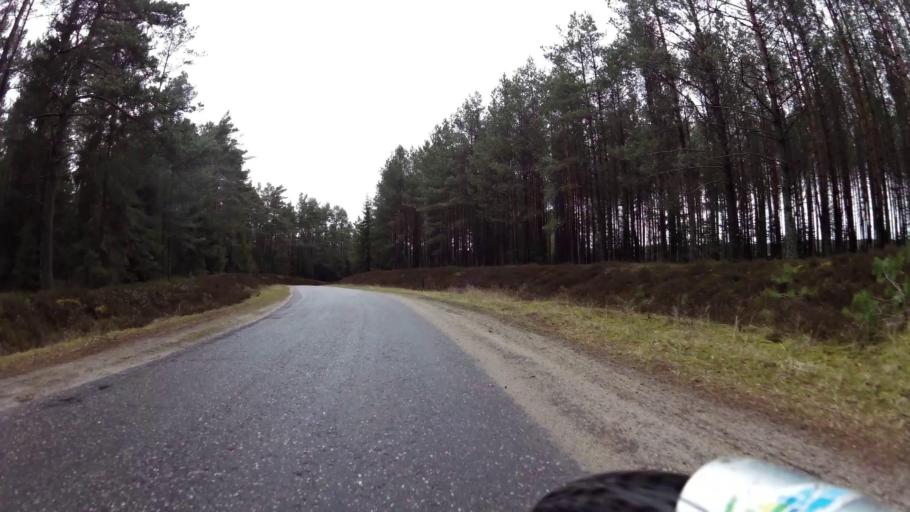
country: PL
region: Pomeranian Voivodeship
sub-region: Powiat bytowski
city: Borzytuchom
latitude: 54.2638
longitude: 17.3667
